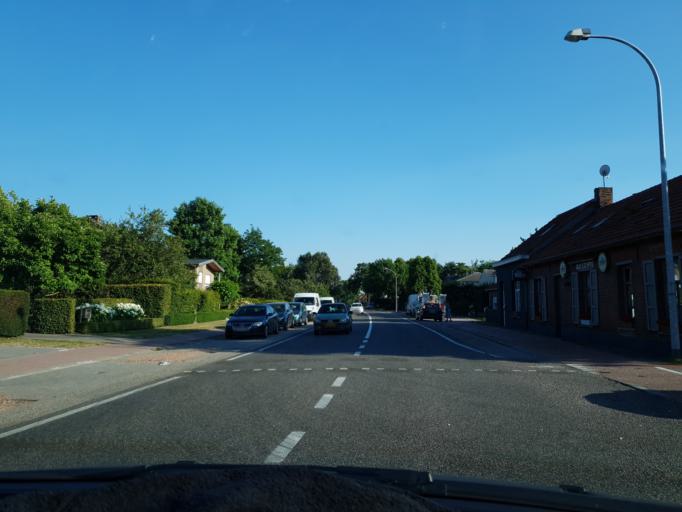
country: BE
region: Flanders
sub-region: Provincie Antwerpen
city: Hoogstraten
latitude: 51.3923
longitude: 4.7554
